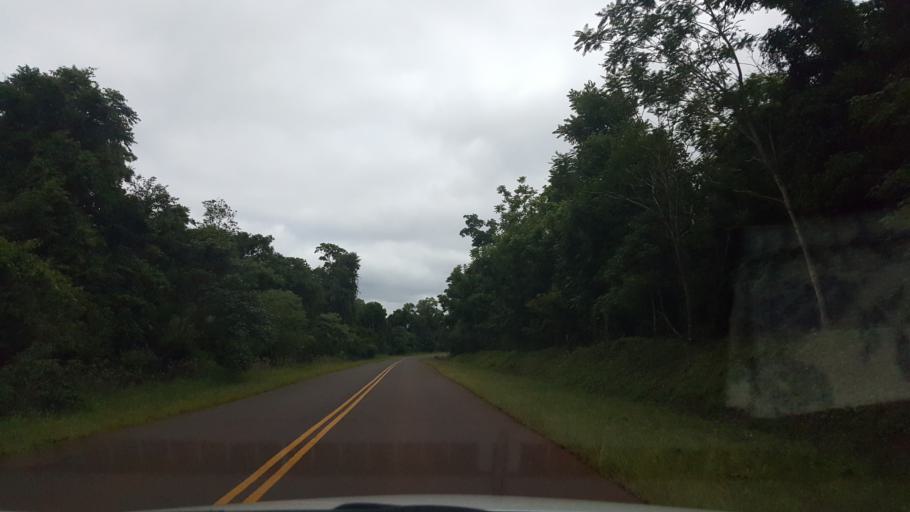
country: AR
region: Misiones
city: Capiovi
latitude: -26.9633
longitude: -55.0901
